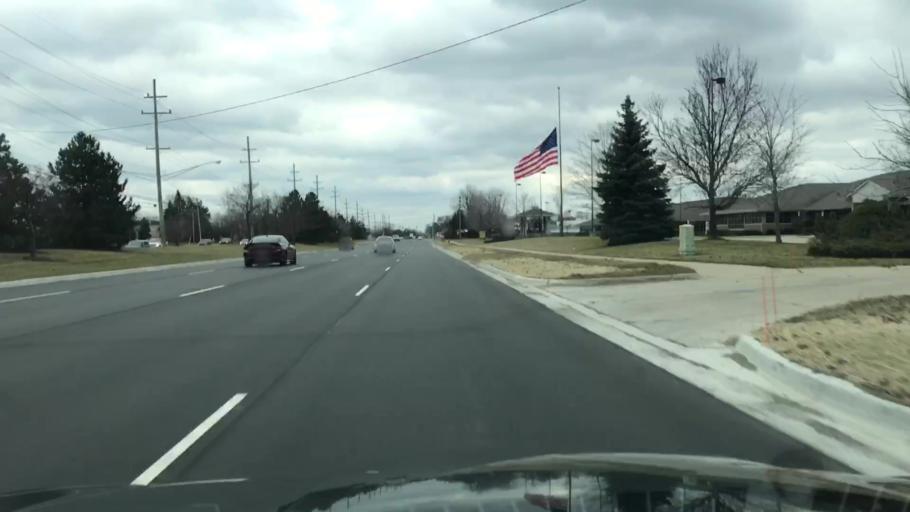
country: US
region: Michigan
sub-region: Macomb County
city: Sterling Heights
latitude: 42.5564
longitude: -83.0493
